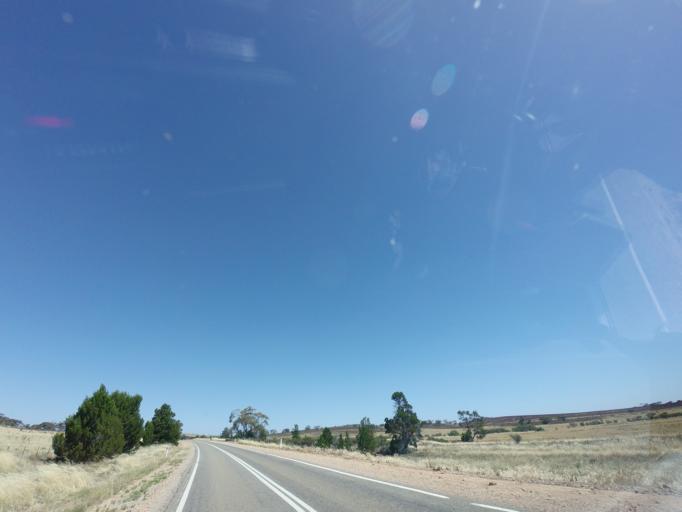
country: AU
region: South Australia
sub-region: Peterborough
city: Peterborough
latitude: -32.9104
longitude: 138.7620
